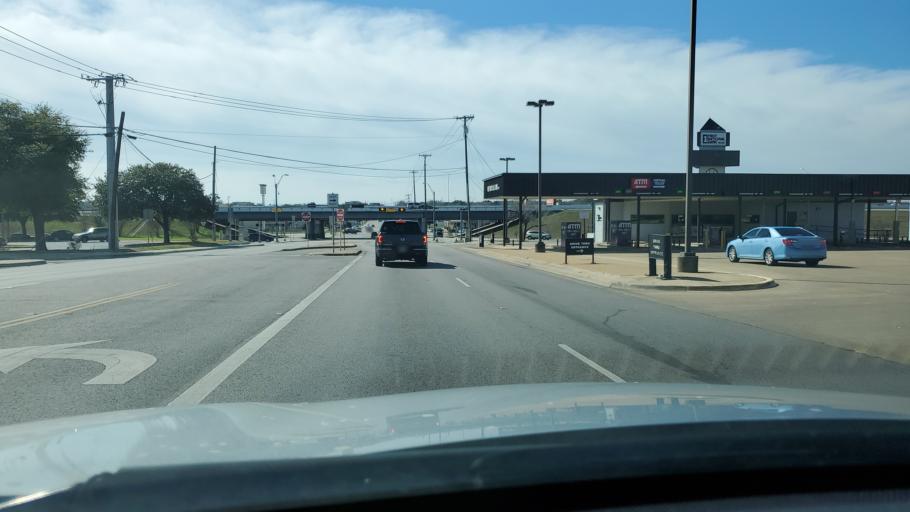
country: US
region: Texas
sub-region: Bell County
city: Killeen
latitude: 31.0963
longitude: -97.7319
